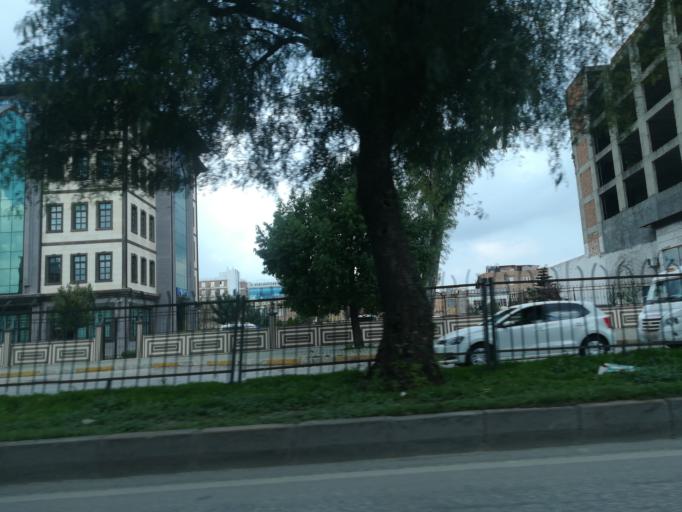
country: TR
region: Adana
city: Seyhan
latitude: 36.9924
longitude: 35.3149
